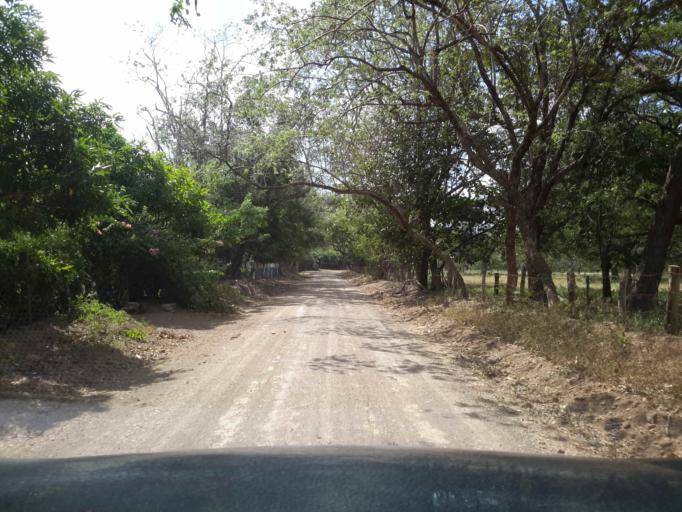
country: NI
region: Rivas
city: San Juan del Sur
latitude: 11.1998
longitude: -85.8048
